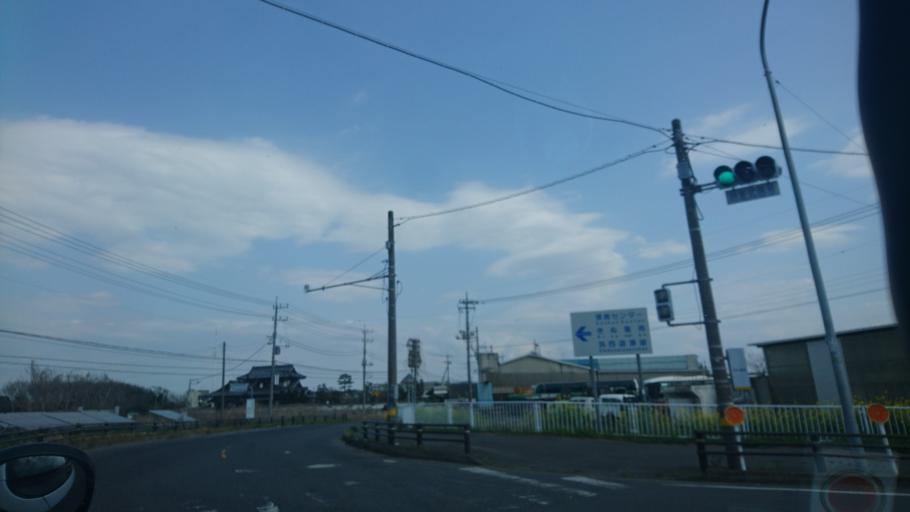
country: JP
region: Ibaraki
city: Yuki
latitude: 36.2942
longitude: 139.9006
